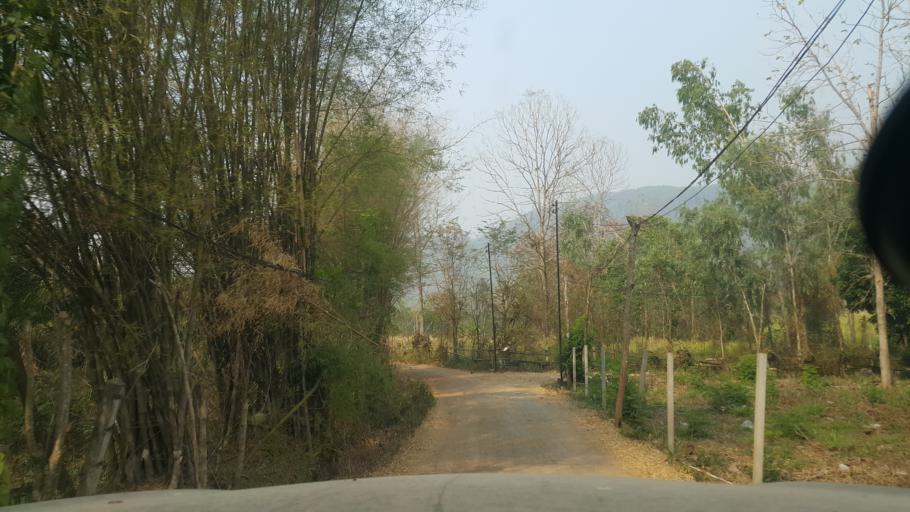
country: TH
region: Chiang Mai
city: Mae On
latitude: 18.7683
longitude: 99.2684
